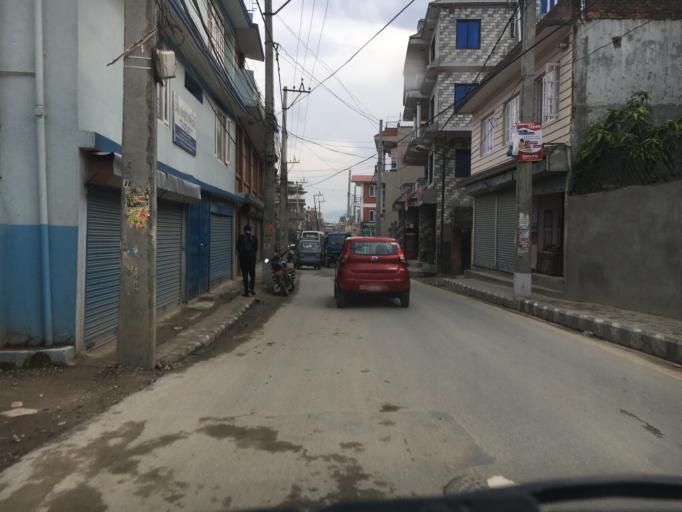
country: NP
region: Central Region
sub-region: Bagmati Zone
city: Kathmandu
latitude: 27.7351
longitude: 85.3466
